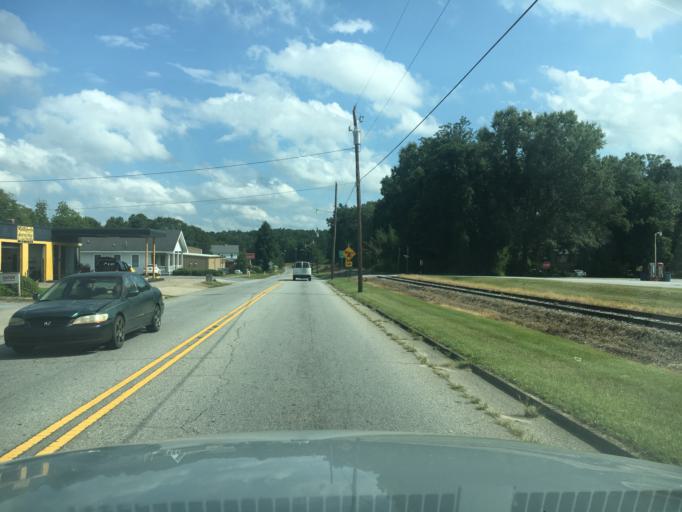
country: US
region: South Carolina
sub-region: Anderson County
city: Belton
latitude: 34.5206
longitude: -82.4924
